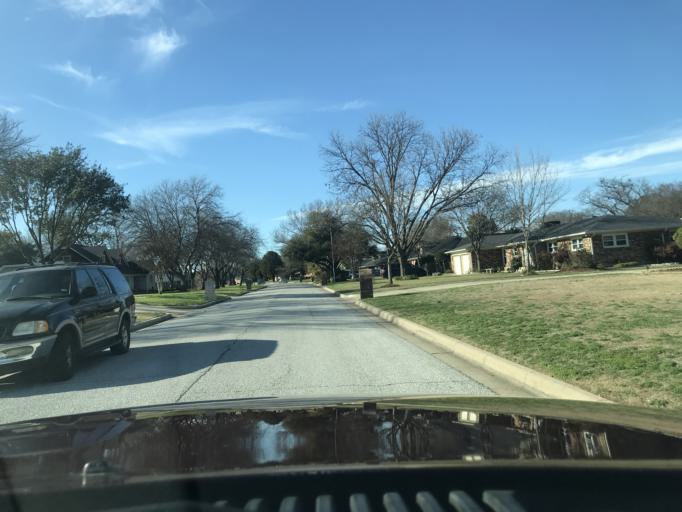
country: US
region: Texas
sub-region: Tarrant County
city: Edgecliff Village
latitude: 32.6565
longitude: -97.3454
